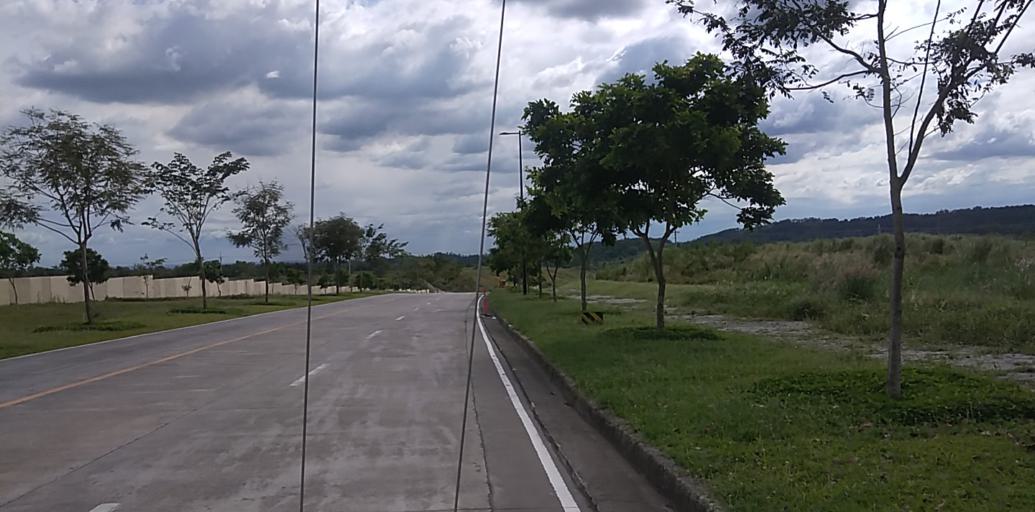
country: PH
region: Central Luzon
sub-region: Province of Pampanga
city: Dolores
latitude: 15.1131
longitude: 120.5131
